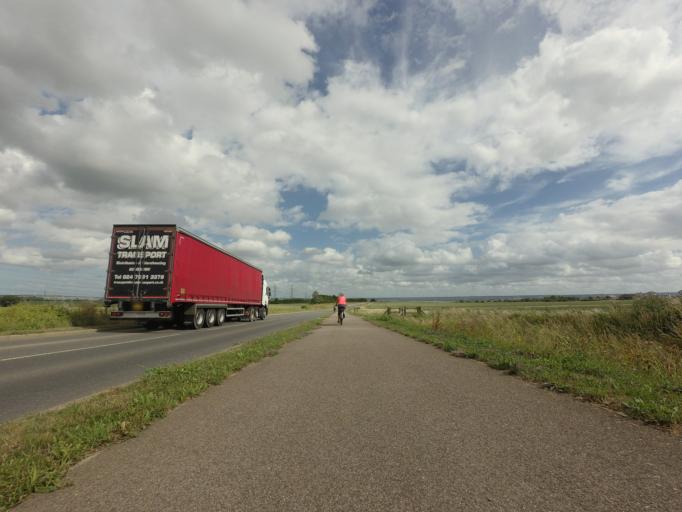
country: GB
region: England
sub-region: Medway
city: High Halstow
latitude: 51.4342
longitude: 0.5699
